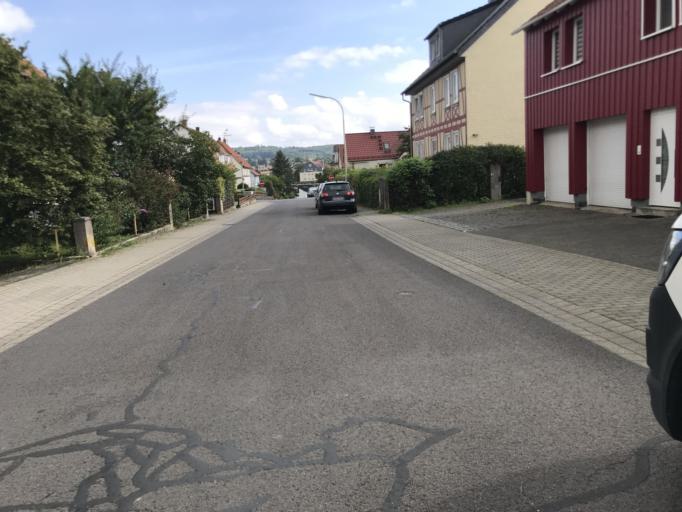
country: DE
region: Hesse
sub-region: Regierungsbezirk Giessen
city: Lauterbach
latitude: 50.6368
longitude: 9.3882
